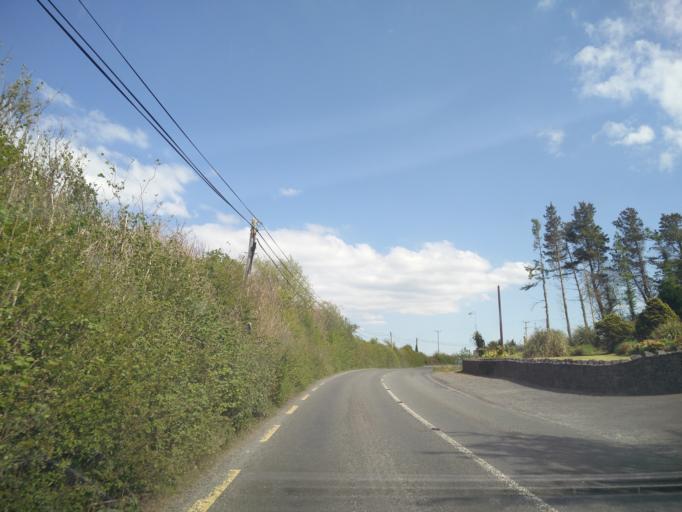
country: IE
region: Connaught
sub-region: Maigh Eo
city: Westport
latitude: 53.7874
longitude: -9.4613
